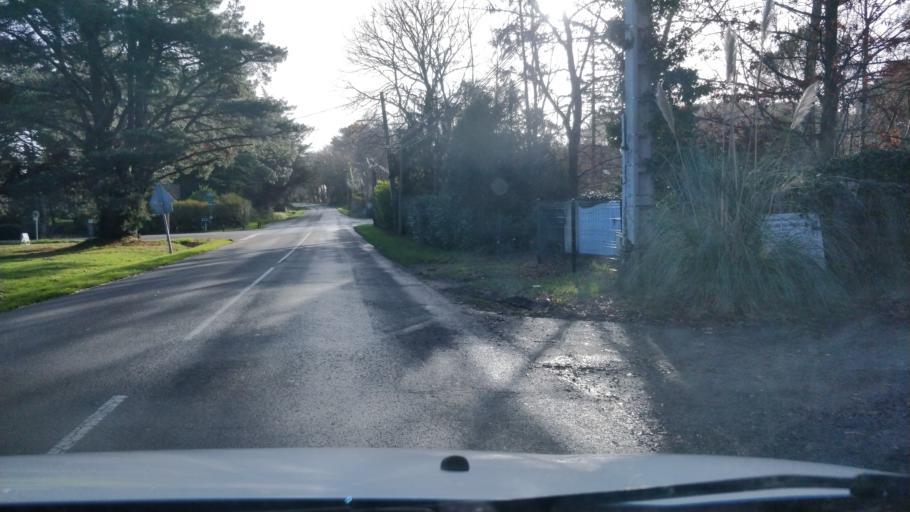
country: FR
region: Pays de la Loire
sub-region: Departement de la Loire-Atlantique
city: Mesquer
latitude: 47.3948
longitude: -2.4661
